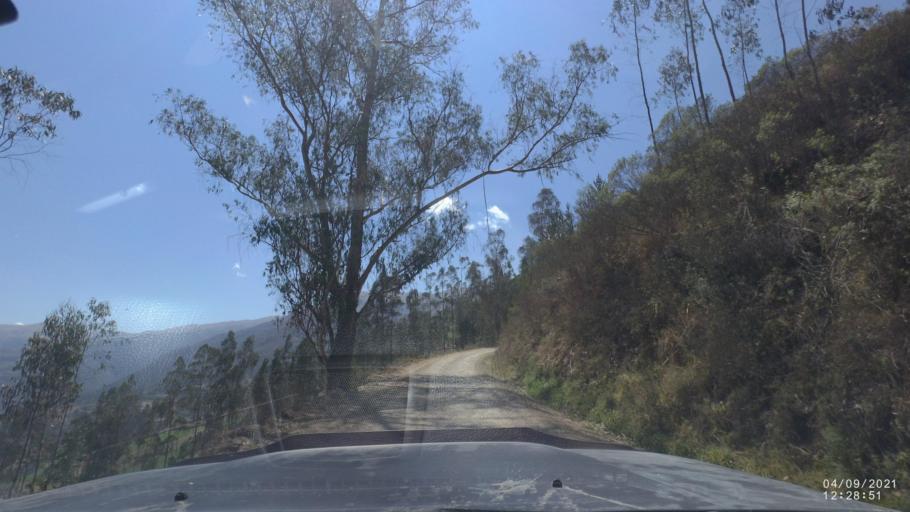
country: BO
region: Cochabamba
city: Colchani
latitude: -17.2277
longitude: -66.5259
